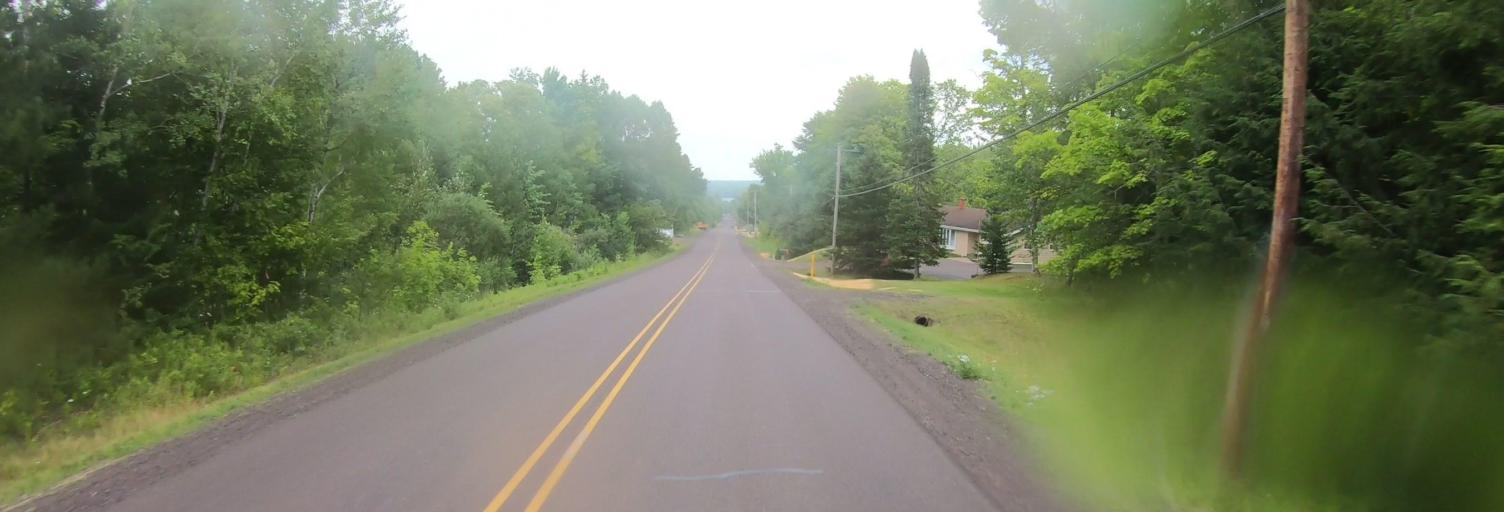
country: US
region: Michigan
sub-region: Houghton County
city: Dollar Bay
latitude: 47.0252
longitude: -88.5386
